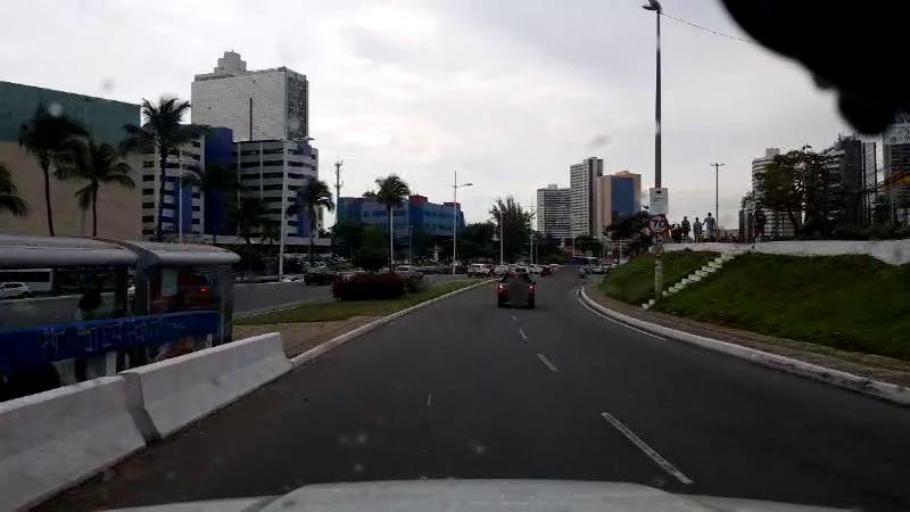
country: BR
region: Bahia
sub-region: Salvador
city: Salvador
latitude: -12.9812
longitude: -38.4664
